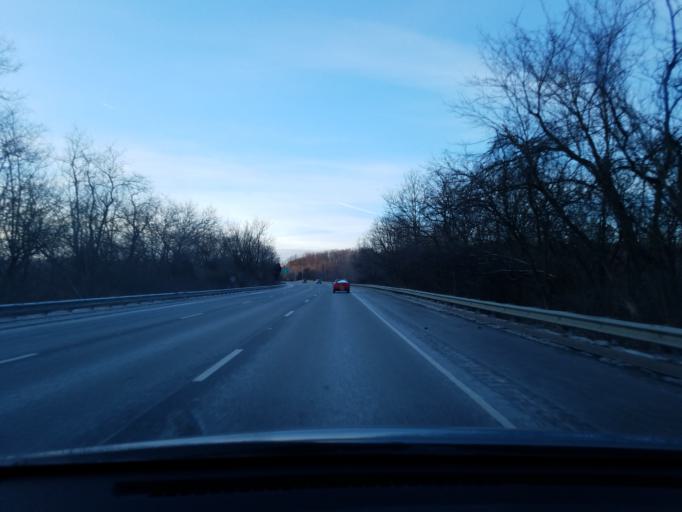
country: US
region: Indiana
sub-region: Floyd County
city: New Albany
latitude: 38.2984
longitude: -85.8438
